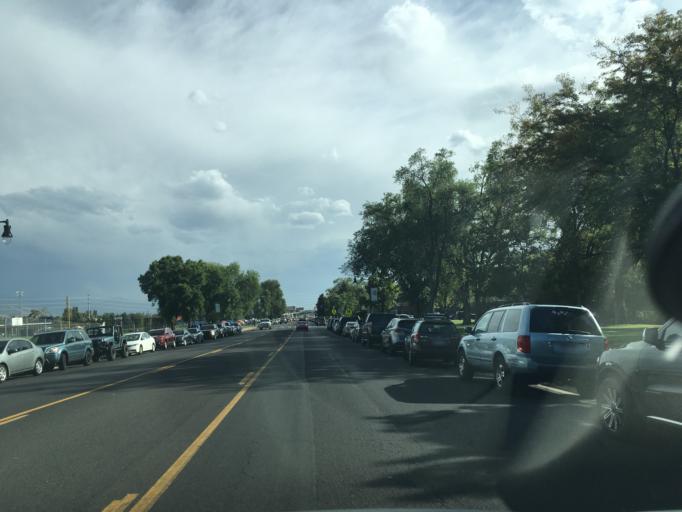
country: US
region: Utah
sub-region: Davis County
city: Layton
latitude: 41.0639
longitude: -111.9614
